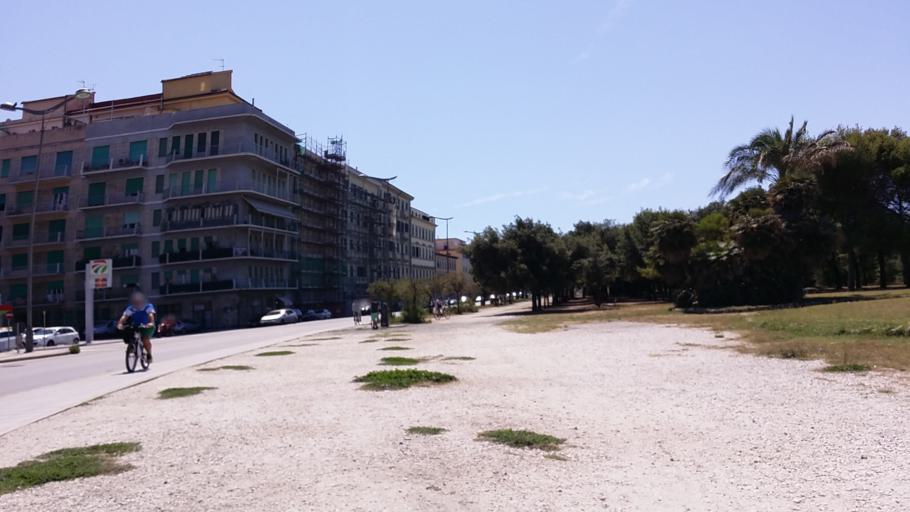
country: IT
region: Tuscany
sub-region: Provincia di Livorno
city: Livorno
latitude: 43.5412
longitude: 10.3016
